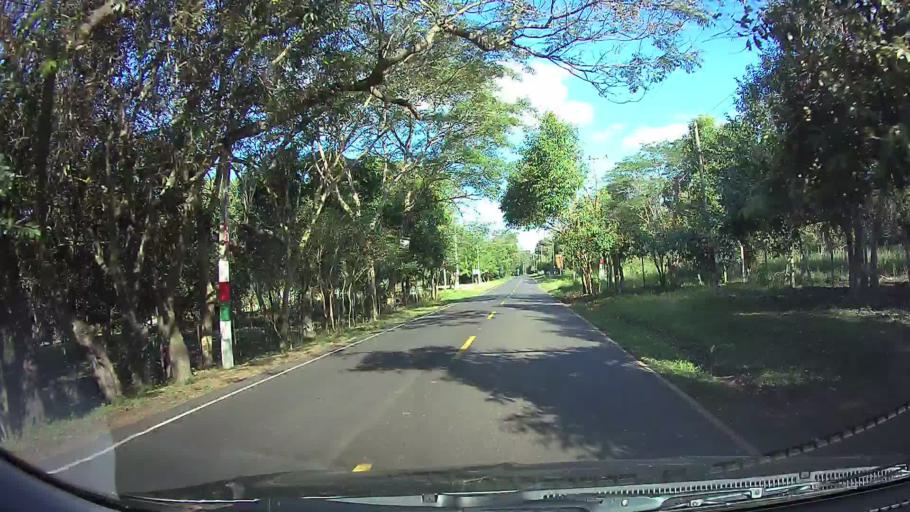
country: PY
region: Central
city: Aregua
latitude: -25.2895
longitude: -57.3947
